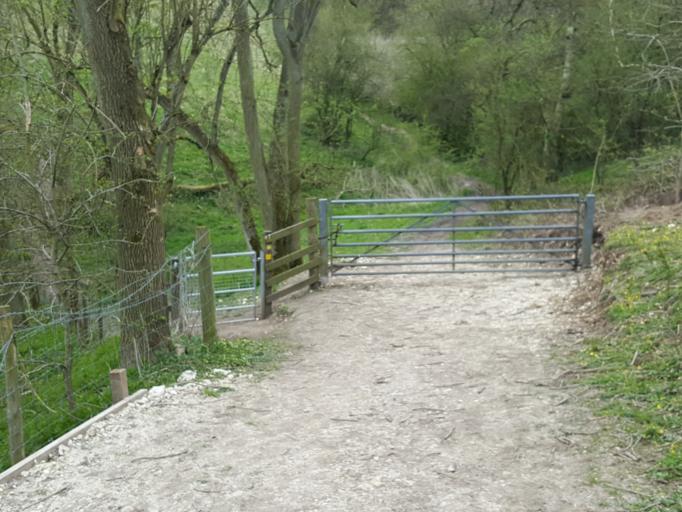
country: GB
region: England
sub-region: East Riding of Yorkshire
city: Brantingham
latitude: 53.7644
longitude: -0.5784
